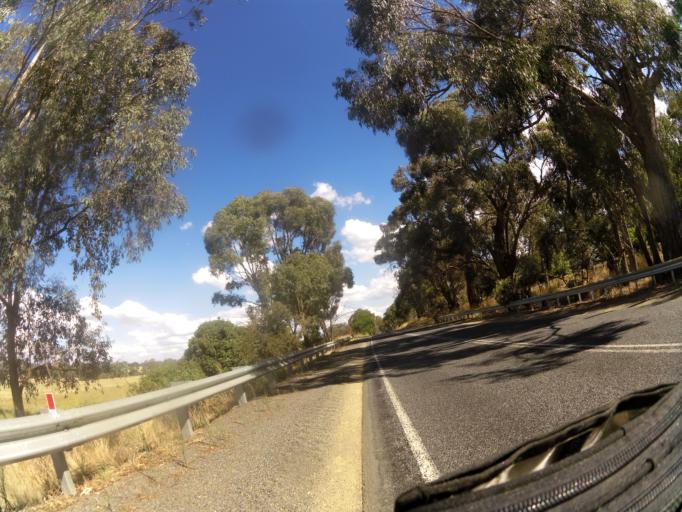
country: AU
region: Victoria
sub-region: Mansfield
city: Mansfield
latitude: -36.9254
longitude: 146.0018
